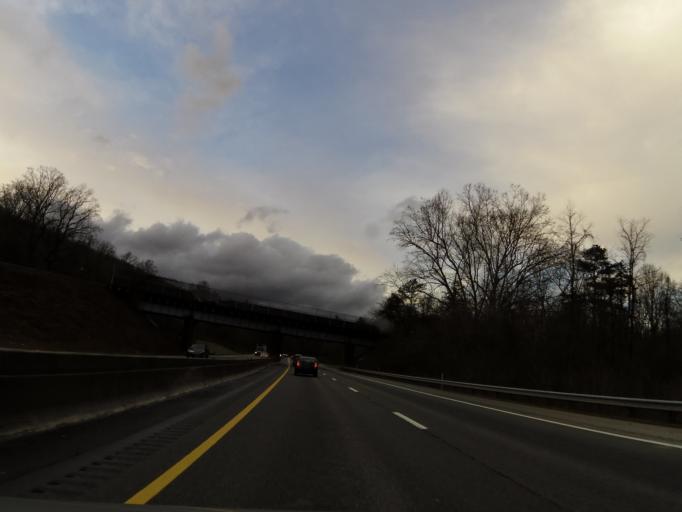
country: US
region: Tennessee
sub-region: Campbell County
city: Caryville
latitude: 36.2624
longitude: -84.1888
